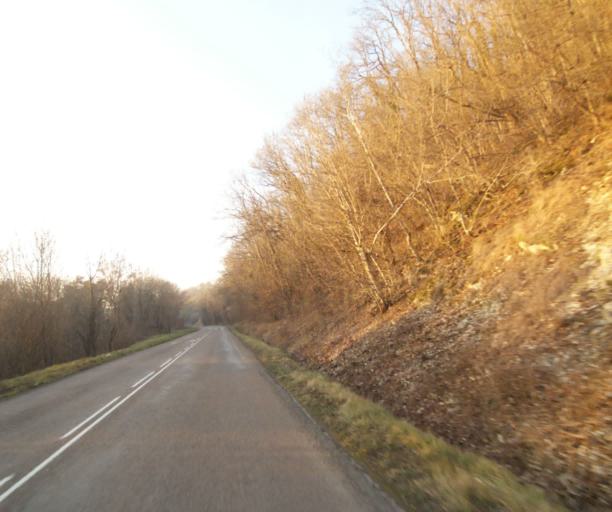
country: FR
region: Lorraine
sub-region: Departement de la Meuse
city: Ancerville
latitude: 48.6125
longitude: 5.0442
